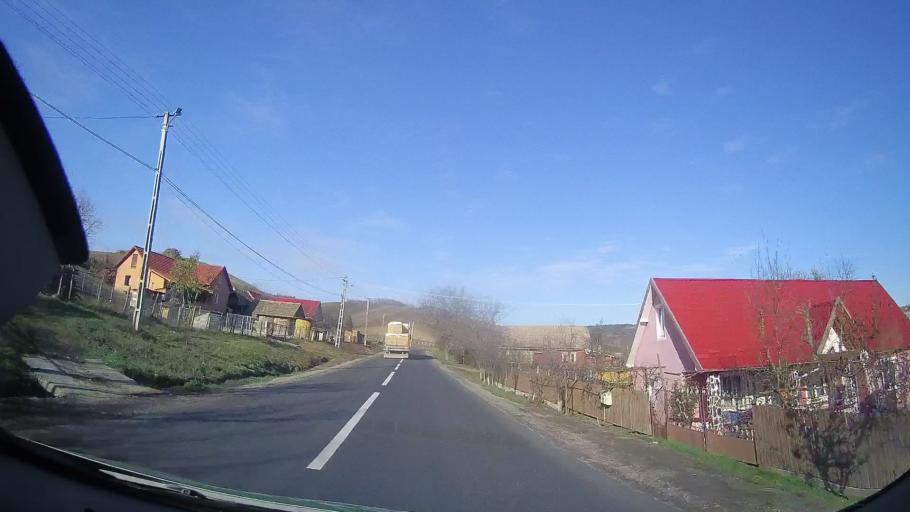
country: RO
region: Mures
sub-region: Comuna Zau De Campie
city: Zau de Campie
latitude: 46.6290
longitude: 24.1327
